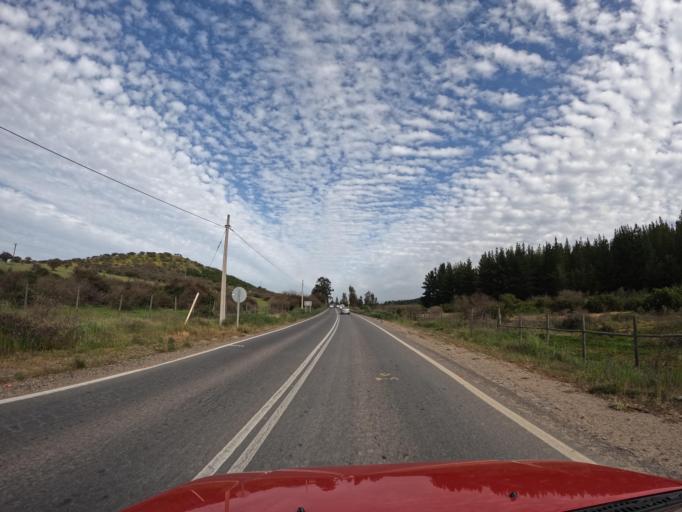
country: CL
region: O'Higgins
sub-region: Provincia de Colchagua
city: Santa Cruz
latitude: -34.3223
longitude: -71.7591
